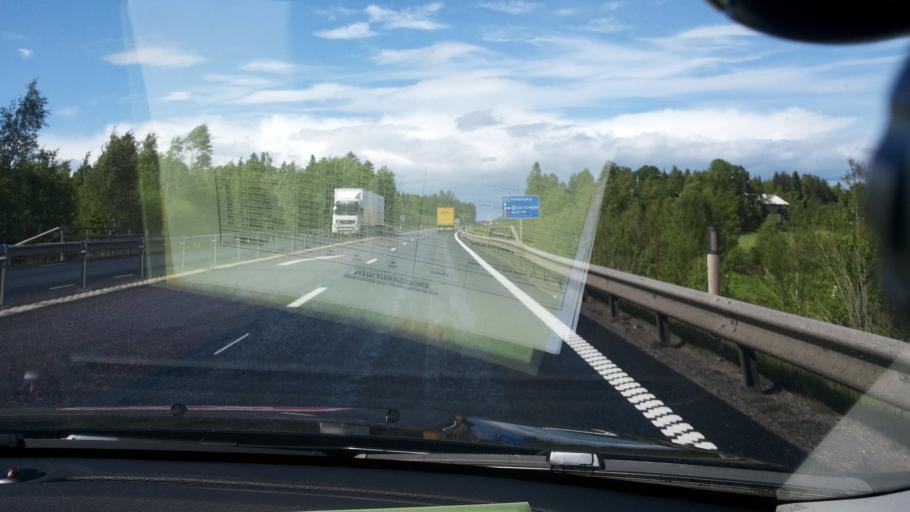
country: SE
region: Vaesternorrland
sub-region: Sundsvalls Kommun
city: Njurundabommen
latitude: 62.2262
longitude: 17.3719
